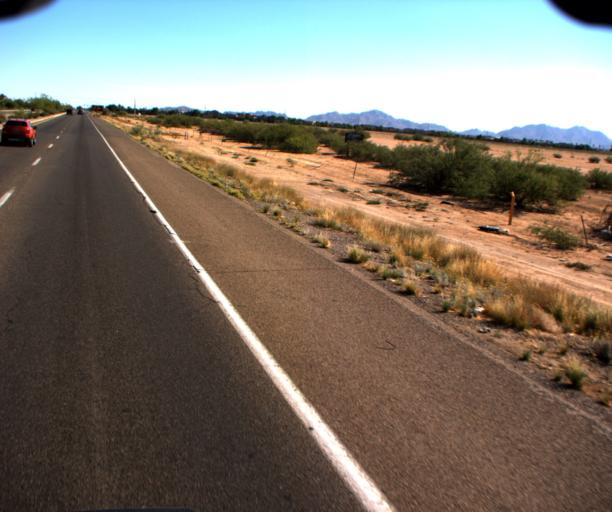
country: US
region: Arizona
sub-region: Pinal County
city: Casa Grande
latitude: 32.9322
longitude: -111.7567
